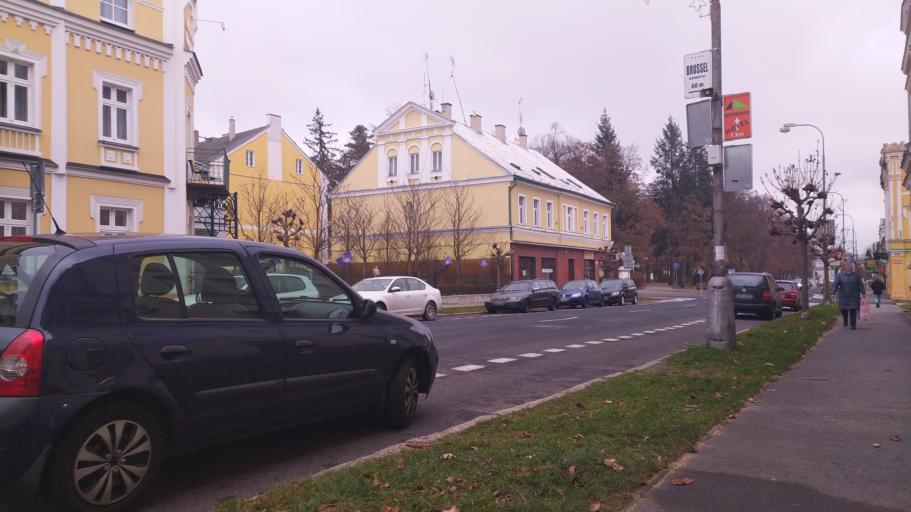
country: CZ
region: Karlovarsky
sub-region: Okres Cheb
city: Frantiskovy Lazne
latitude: 50.1229
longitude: 12.3480
